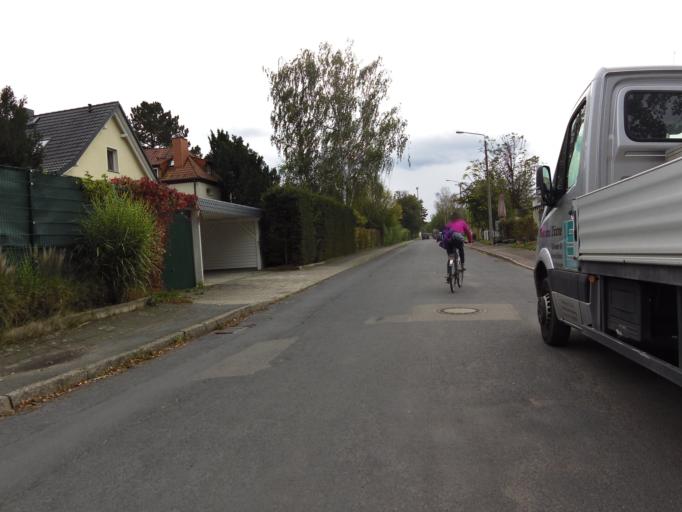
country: DE
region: Saxony
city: Markkleeberg
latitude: 51.2926
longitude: 12.3595
